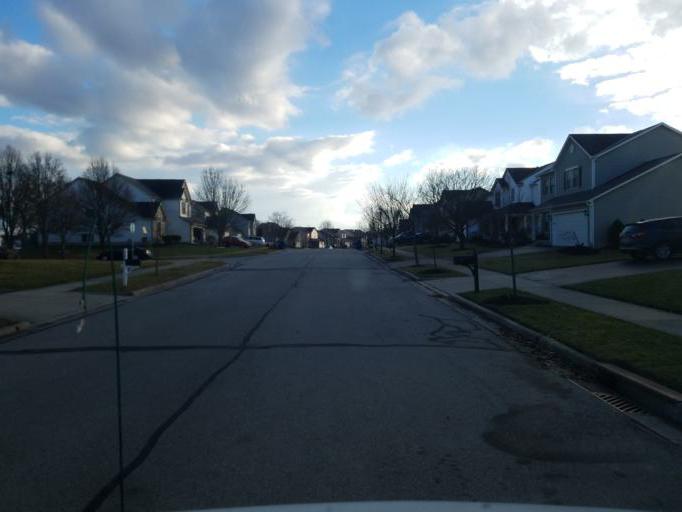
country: US
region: Ohio
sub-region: Delaware County
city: Delaware
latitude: 40.3140
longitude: -83.1037
